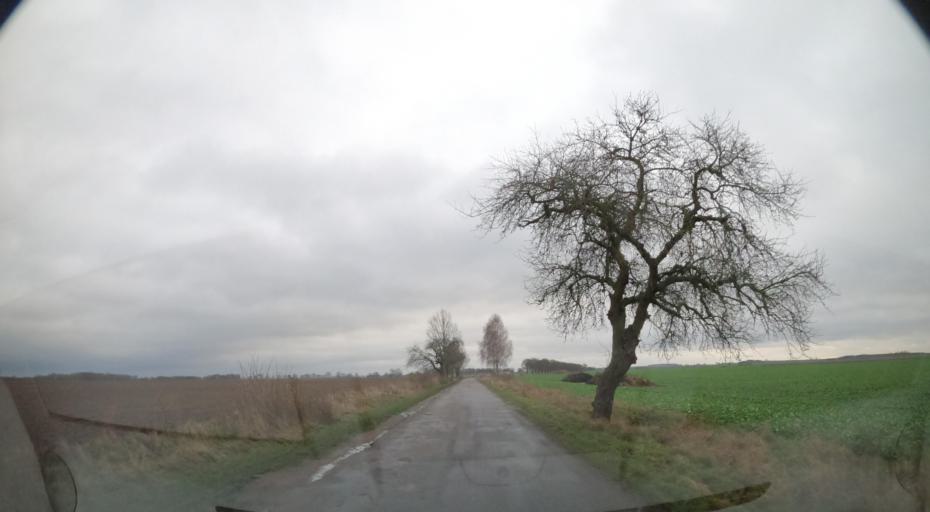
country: PL
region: Greater Poland Voivodeship
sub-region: Powiat pilski
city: Wysoka
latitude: 53.2783
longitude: 17.0927
